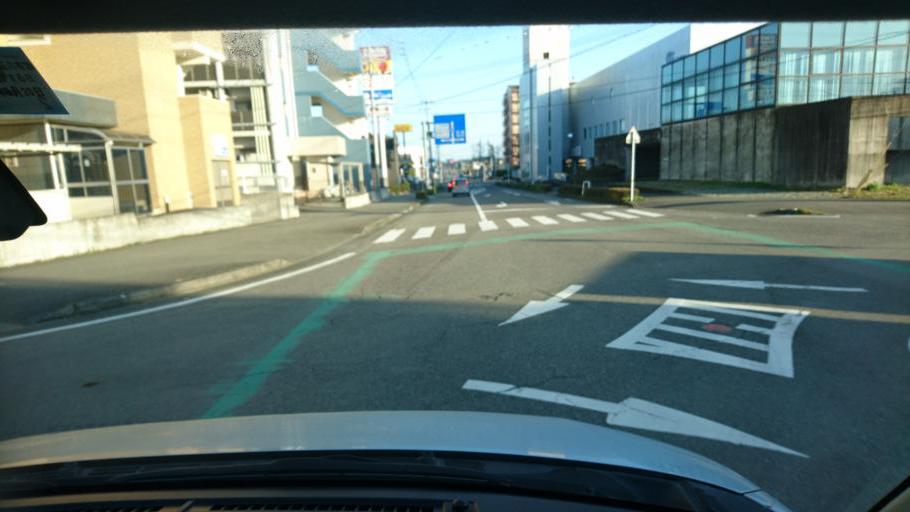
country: JP
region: Miyazaki
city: Miyazaki-shi
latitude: 31.8302
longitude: 131.4202
